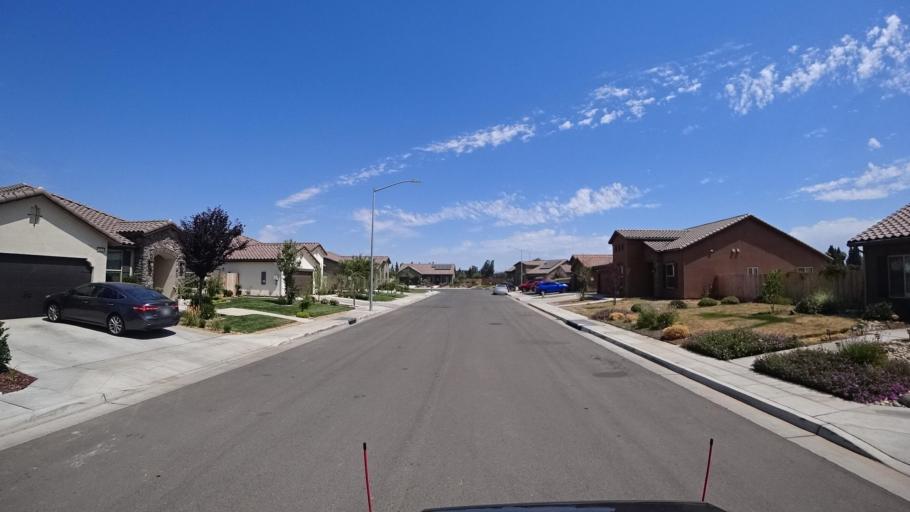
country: US
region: California
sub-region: Fresno County
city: Sunnyside
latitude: 36.7324
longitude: -119.7119
